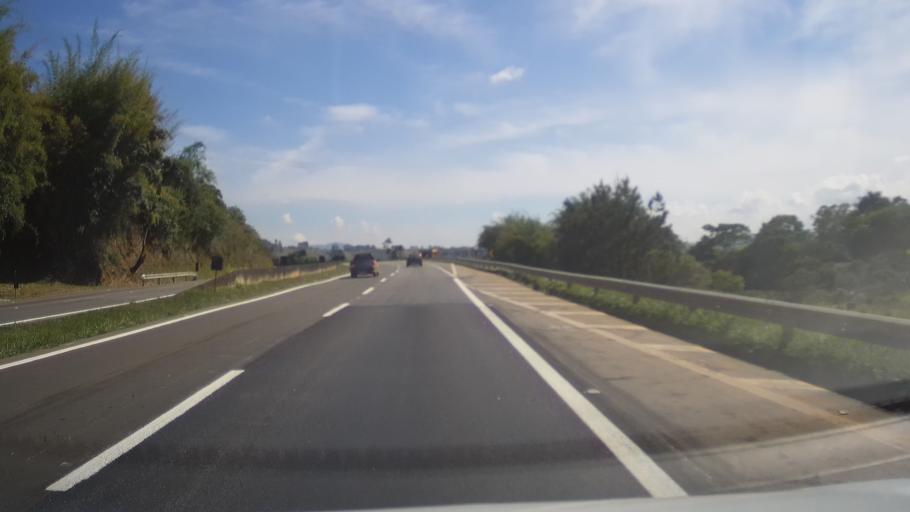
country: BR
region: Minas Gerais
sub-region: Cambui
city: Cambui
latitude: -22.5560
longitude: -46.0397
